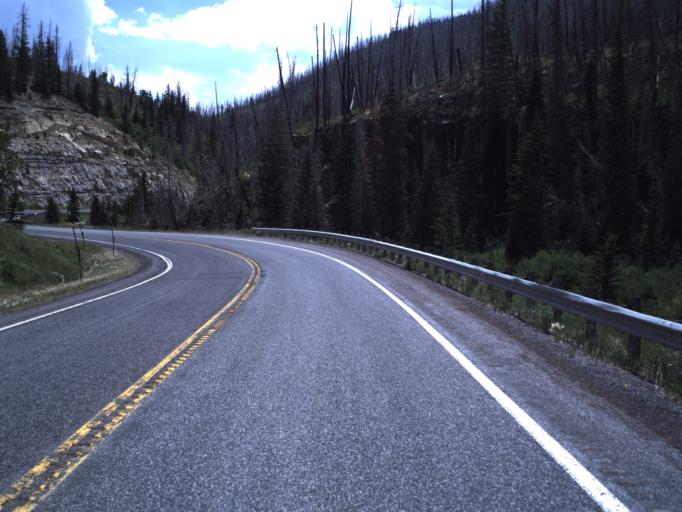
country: US
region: Utah
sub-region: Sanpete County
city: Fairview
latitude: 39.5892
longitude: -111.1941
